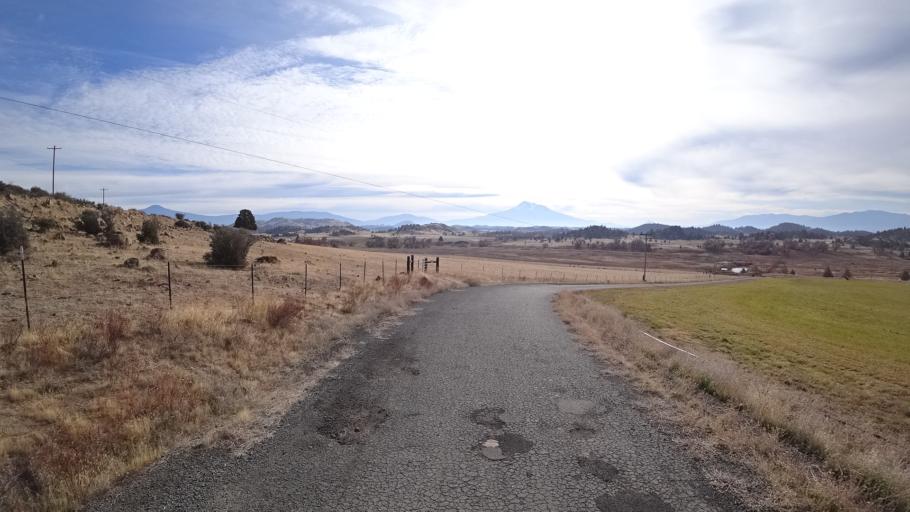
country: US
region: California
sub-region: Siskiyou County
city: Montague
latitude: 41.7075
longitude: -122.5157
